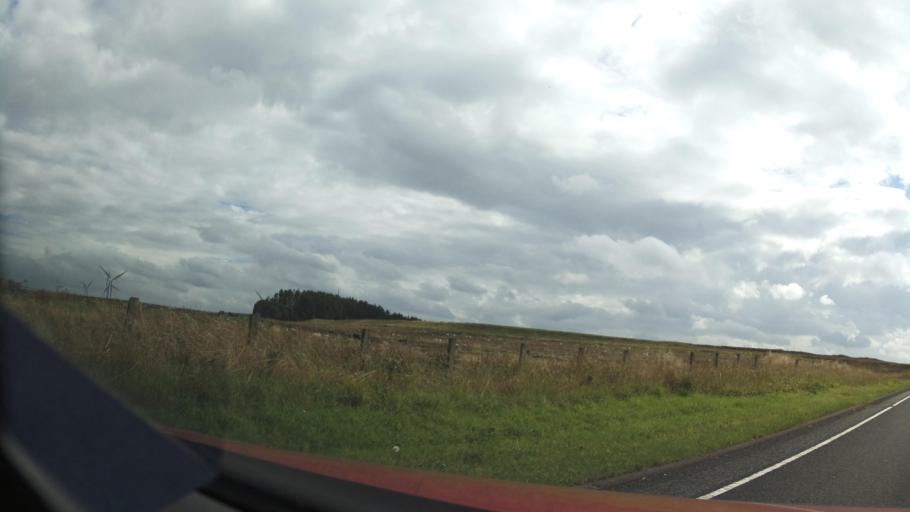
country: GB
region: England
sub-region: Northumberland
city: Corsenside
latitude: 55.1304
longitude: -2.1453
